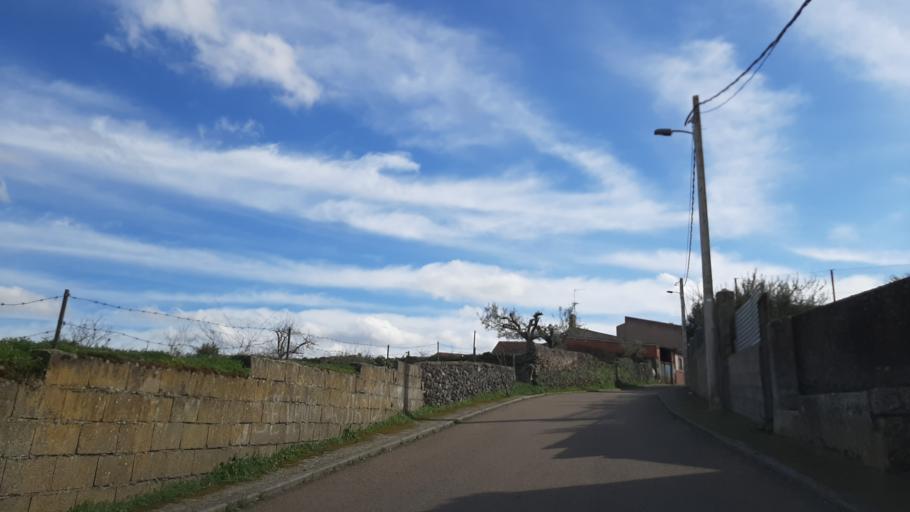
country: ES
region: Castille and Leon
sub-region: Provincia de Salamanca
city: Villarino de los Aires
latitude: 41.2426
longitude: -6.5237
